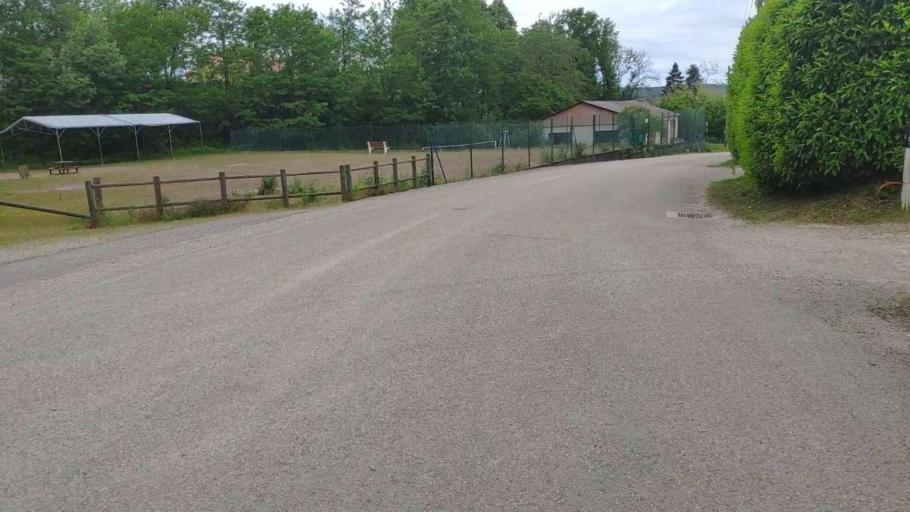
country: FR
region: Franche-Comte
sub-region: Departement du Jura
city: Montmorot
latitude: 46.7540
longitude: 5.5613
